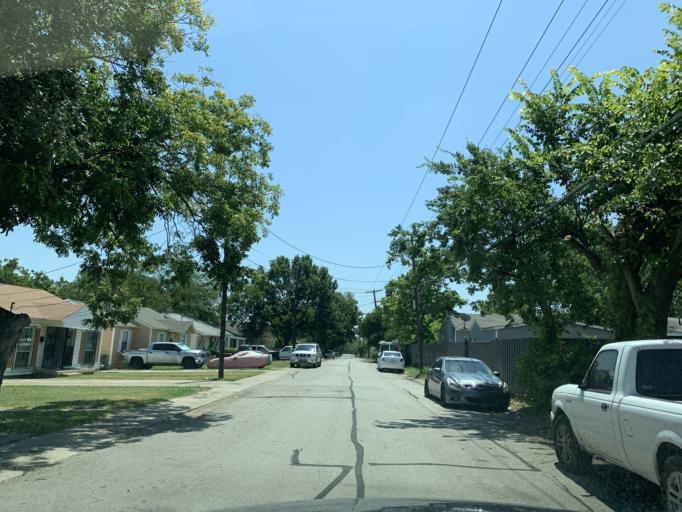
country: US
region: Texas
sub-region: Dallas County
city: Hutchins
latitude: 32.6886
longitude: -96.7974
